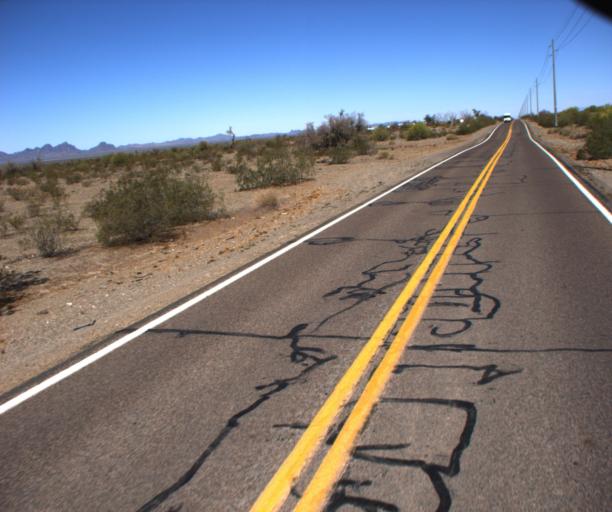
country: US
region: Arizona
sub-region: La Paz County
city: Salome
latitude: 33.7733
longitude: -113.7965
